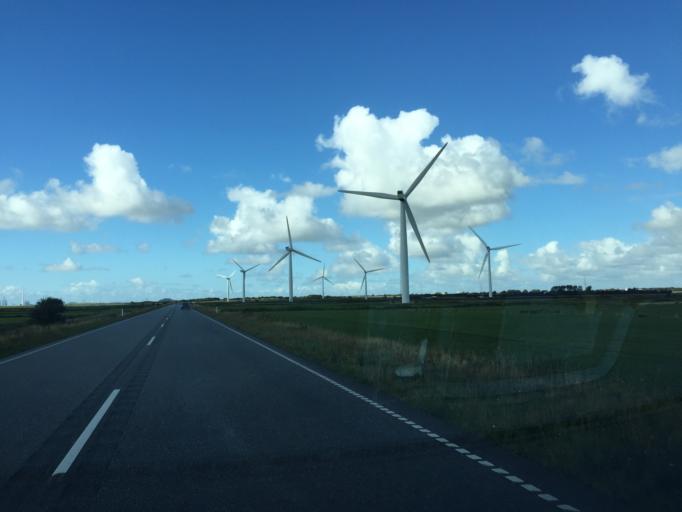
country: DK
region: South Denmark
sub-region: Esbjerg Kommune
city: Tjaereborg
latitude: 55.4430
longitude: 8.6014
